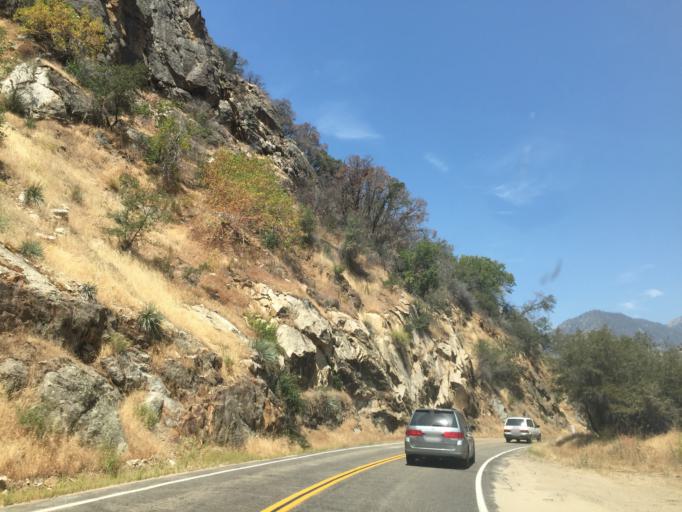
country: US
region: California
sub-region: Tulare County
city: Three Rivers
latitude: 36.8261
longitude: -118.8549
